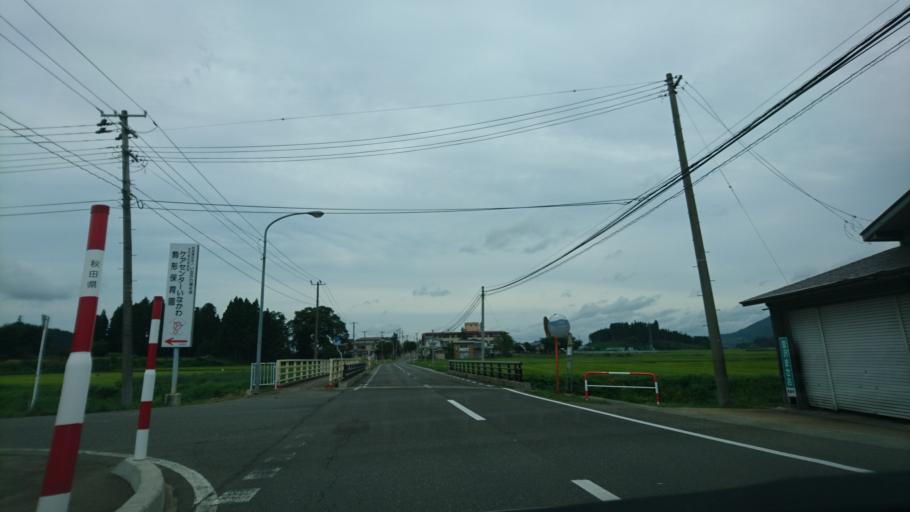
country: JP
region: Akita
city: Yuzawa
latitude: 39.1729
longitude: 140.5567
